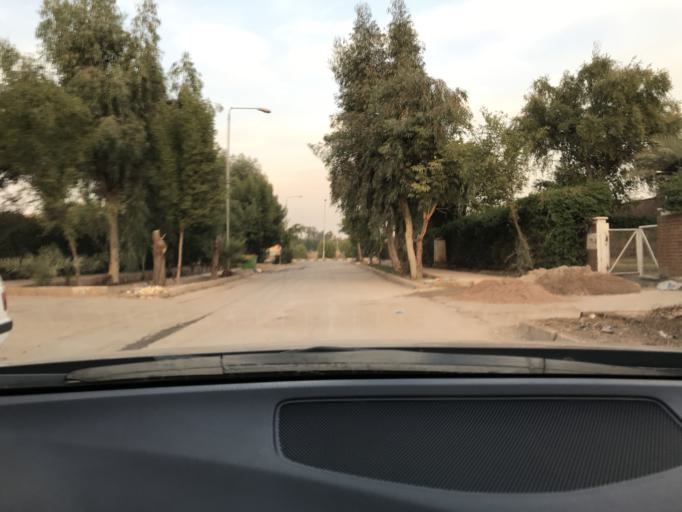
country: IR
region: Khuzestan
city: Ahvaz
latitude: 31.3324
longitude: 48.7331
